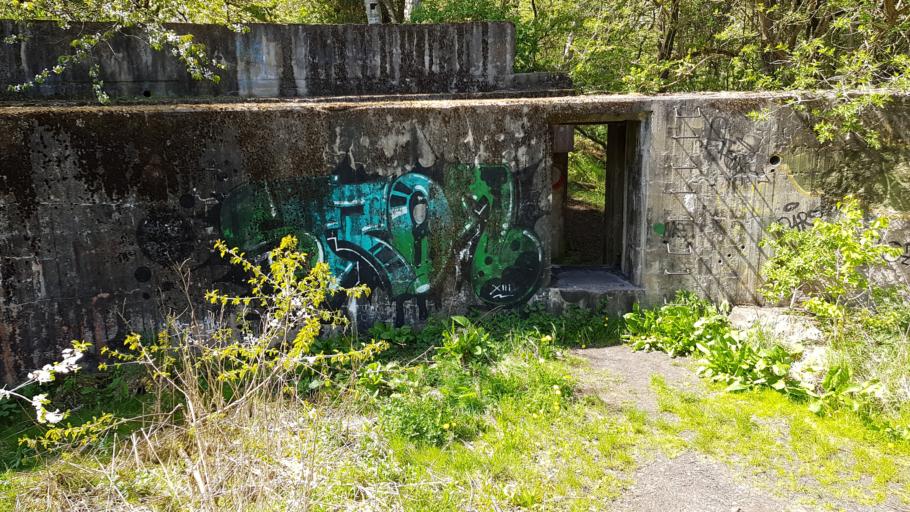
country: DK
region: Capital Region
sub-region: Bornholm Kommune
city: Nexo
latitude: 55.0024
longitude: 15.0839
